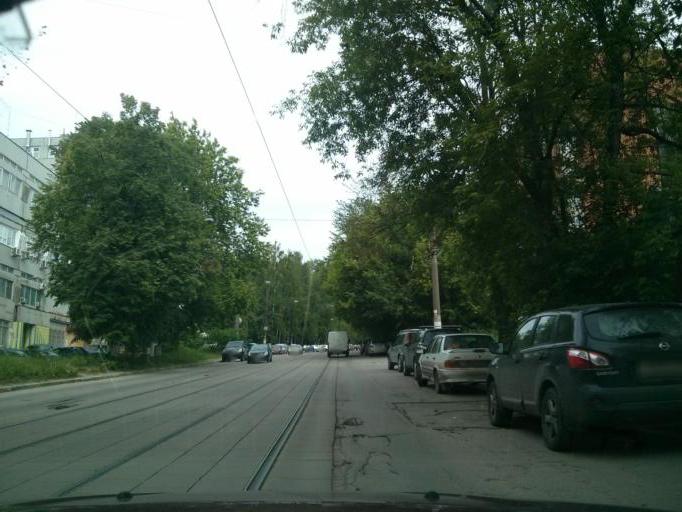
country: RU
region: Nizjnij Novgorod
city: Nizhniy Novgorod
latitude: 56.3079
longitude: 44.0188
